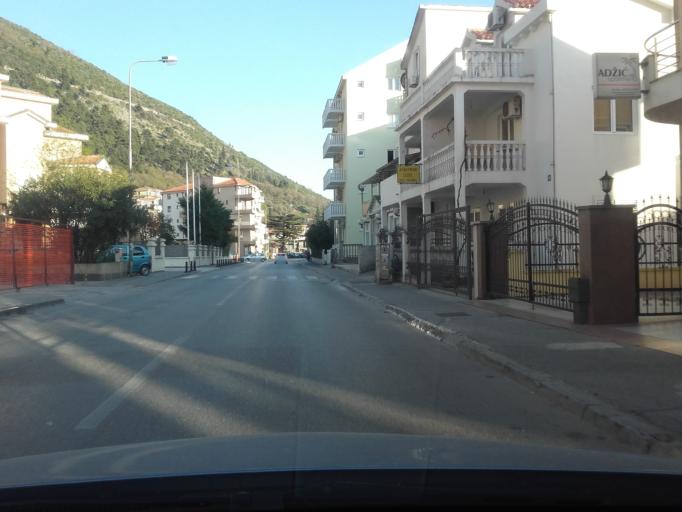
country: ME
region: Budva
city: Budva
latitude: 42.2922
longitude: 18.8491
